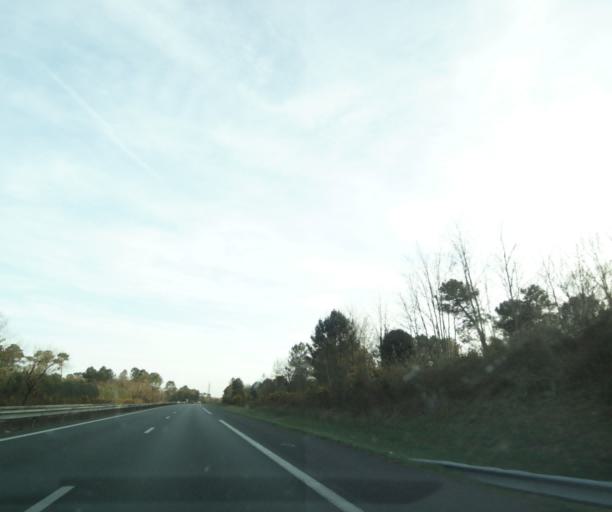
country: FR
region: Aquitaine
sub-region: Departement de la Gironde
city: Saint-Savin
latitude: 45.1675
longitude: -0.4816
